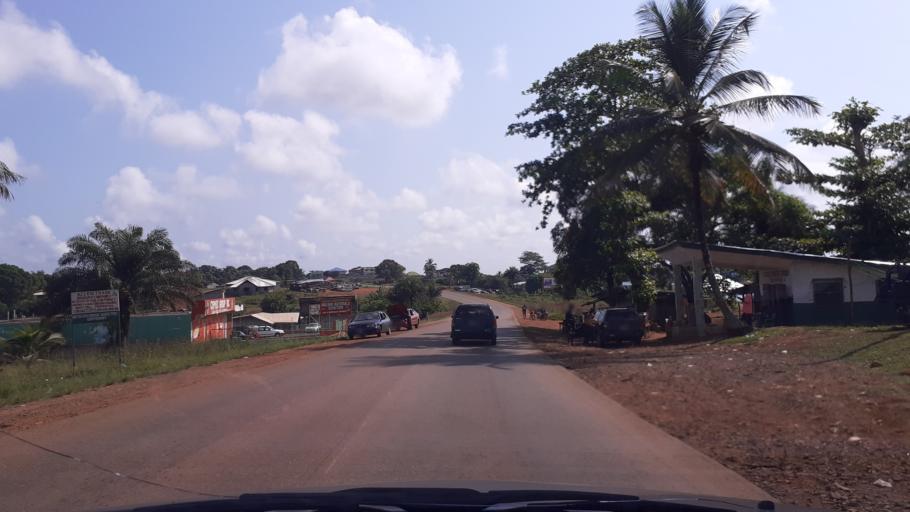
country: LR
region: Montserrado
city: Bensonville City
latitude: 6.2225
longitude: -10.5389
